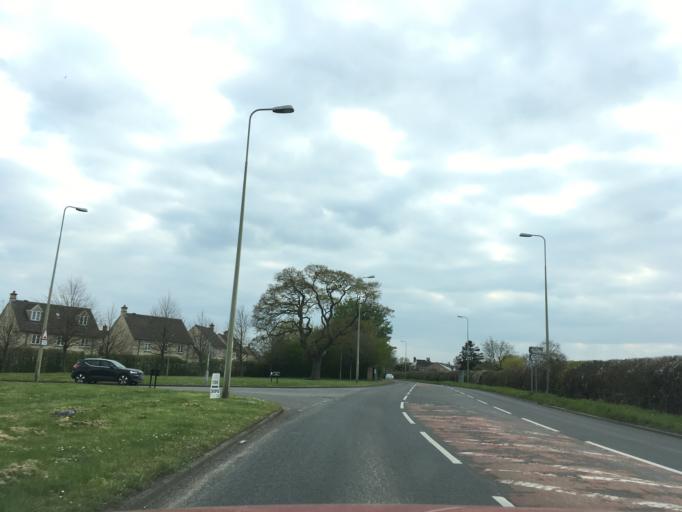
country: GB
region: England
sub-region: Oxfordshire
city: Witney
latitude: 51.7969
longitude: -1.4670
